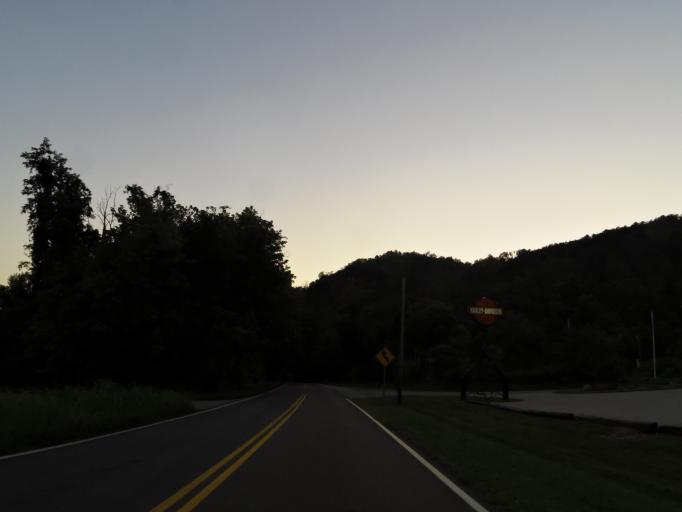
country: US
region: Tennessee
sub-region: Loudon County
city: Greenback
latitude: 35.5475
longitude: -84.0665
